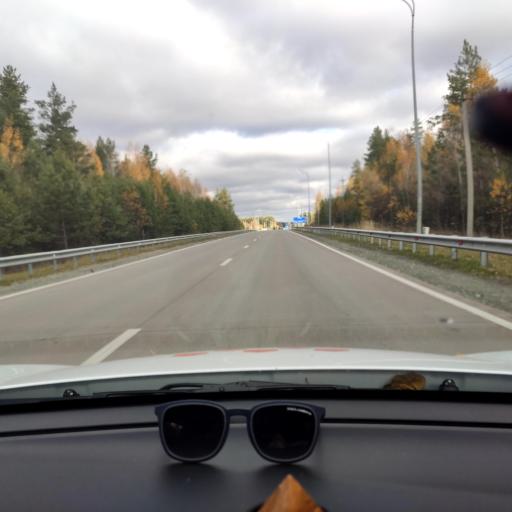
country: RU
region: Tatarstan
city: Stolbishchi
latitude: 55.6372
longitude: 49.1095
